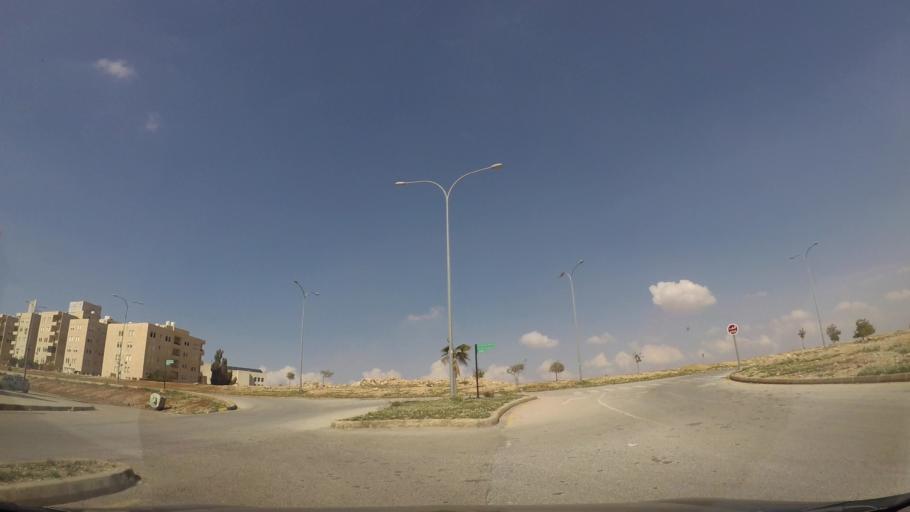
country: JO
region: Zarqa
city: Zarqa
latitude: 32.0708
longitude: 36.1123
